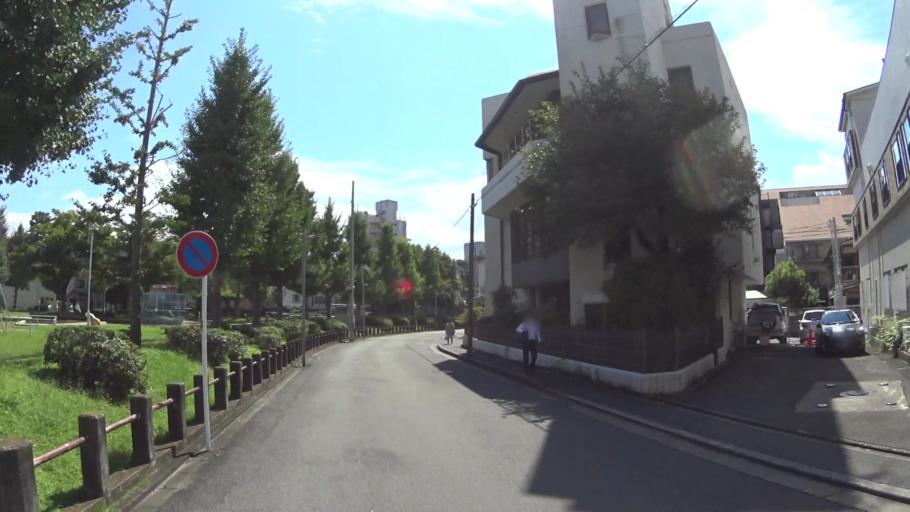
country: JP
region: Kyoto
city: Muko
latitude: 34.9939
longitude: 135.7180
